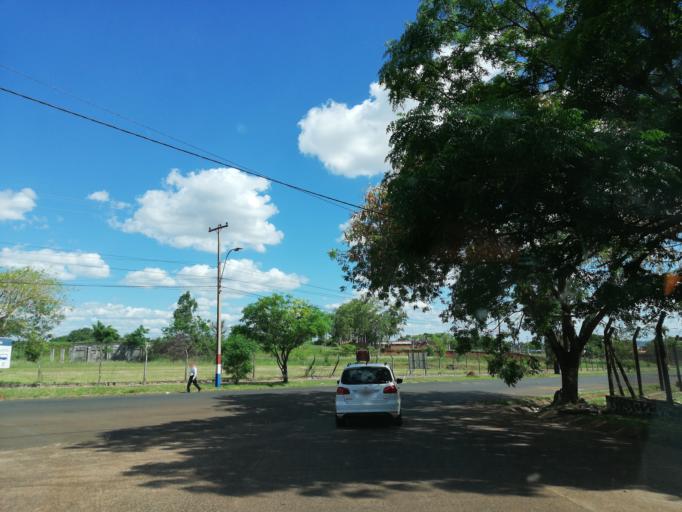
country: PY
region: Itapua
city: Encarnacion
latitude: -27.3644
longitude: -55.8540
